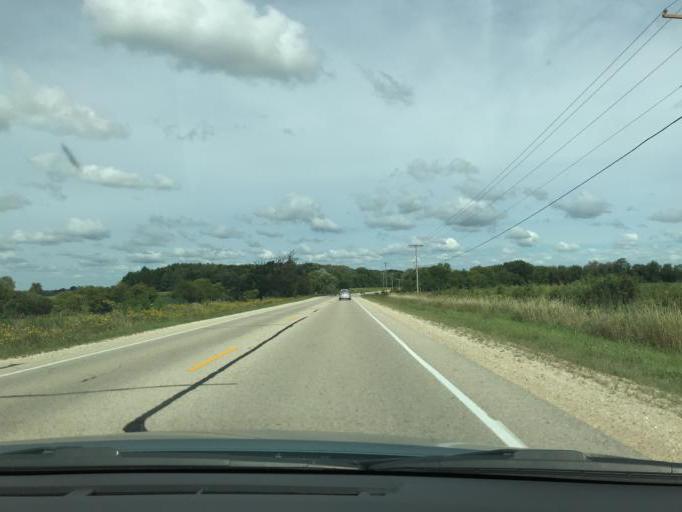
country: US
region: Wisconsin
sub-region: Racine County
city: Bohners Lake
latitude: 42.6269
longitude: -88.2439
